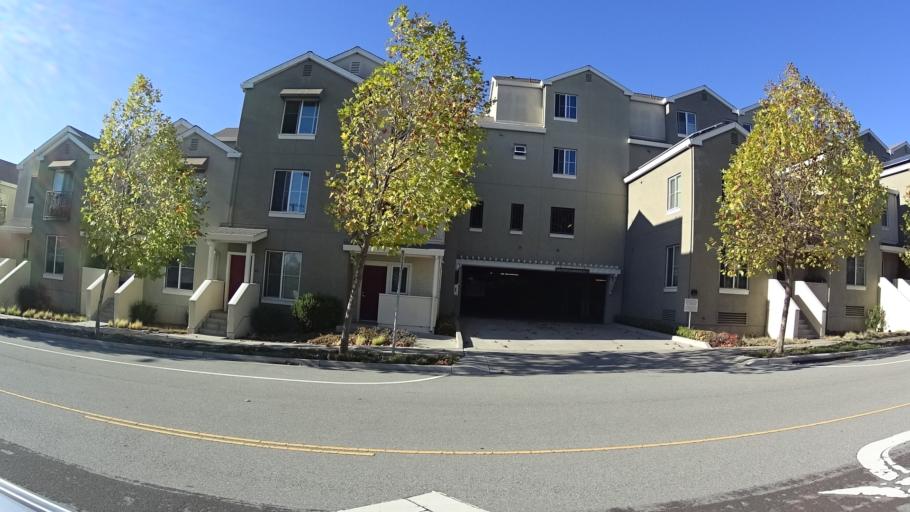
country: US
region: California
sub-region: San Mateo County
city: South San Francisco
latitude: 37.6589
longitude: -122.4325
